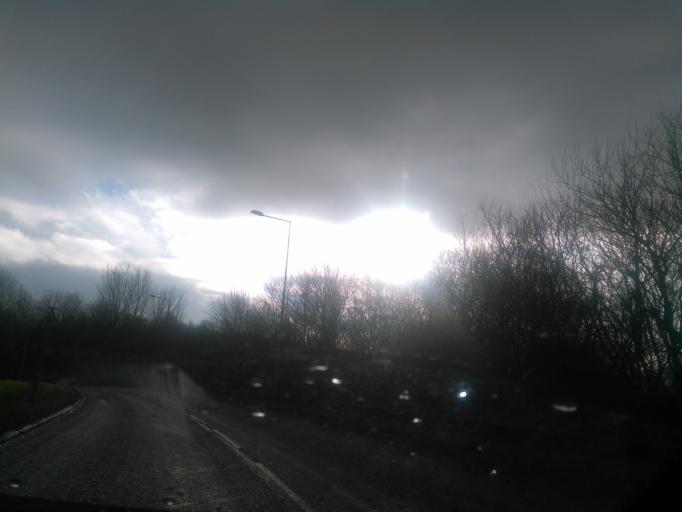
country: GB
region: England
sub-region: Telford and Wrekin
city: Oakengates
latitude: 52.7014
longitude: -2.4641
